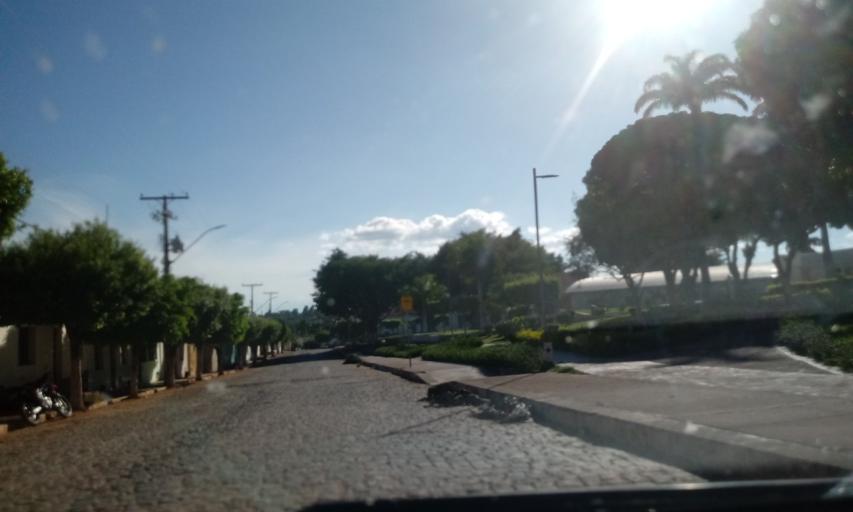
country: BR
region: Bahia
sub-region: Riacho De Santana
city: Riacho de Santana
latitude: -13.7729
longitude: -42.7152
